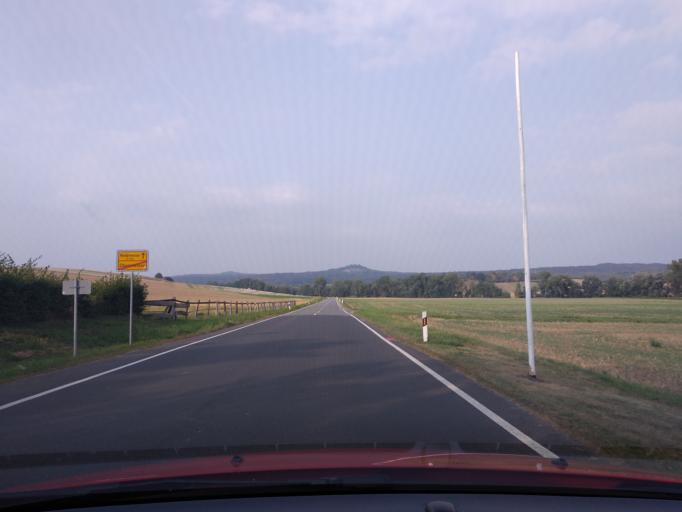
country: DE
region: Hesse
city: Liebenau
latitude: 51.4443
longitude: 9.3038
